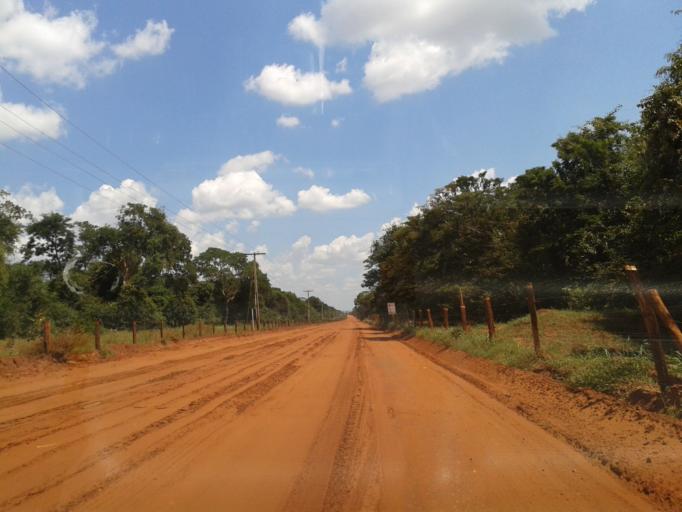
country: BR
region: Minas Gerais
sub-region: Ituiutaba
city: Ituiutaba
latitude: -18.9973
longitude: -49.6633
